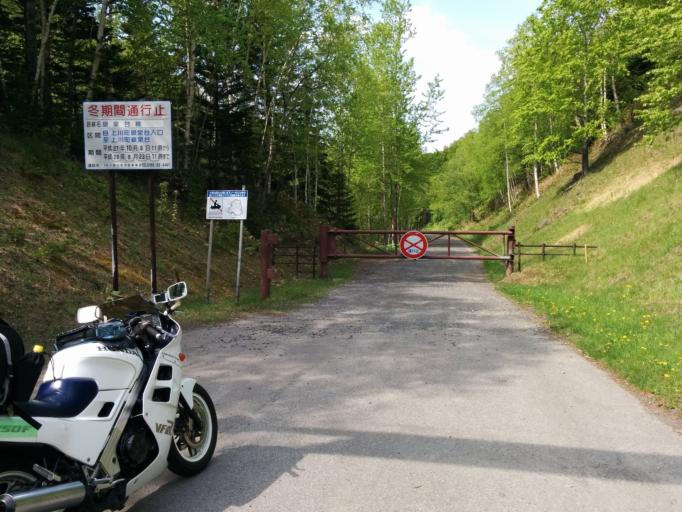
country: JP
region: Hokkaido
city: Kamikawa
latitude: 43.6623
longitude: 143.0348
